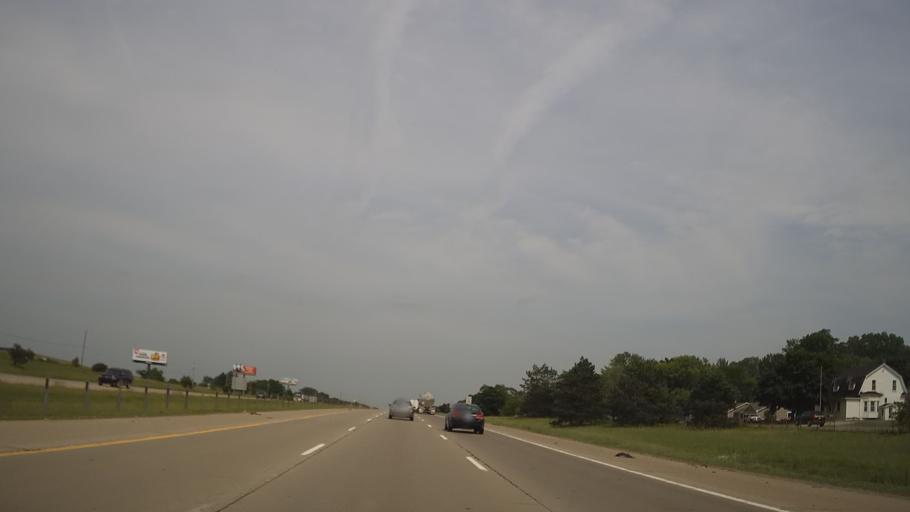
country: US
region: Michigan
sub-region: Wayne County
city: Belleville
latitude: 42.2187
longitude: -83.5339
